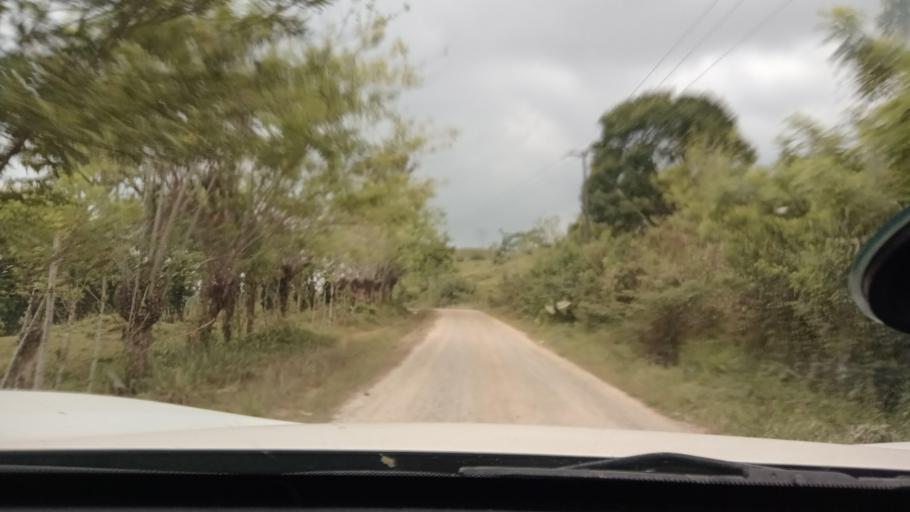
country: MX
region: Tabasco
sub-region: Huimanguillo
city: Francisco Rueda
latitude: 17.4373
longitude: -94.0570
